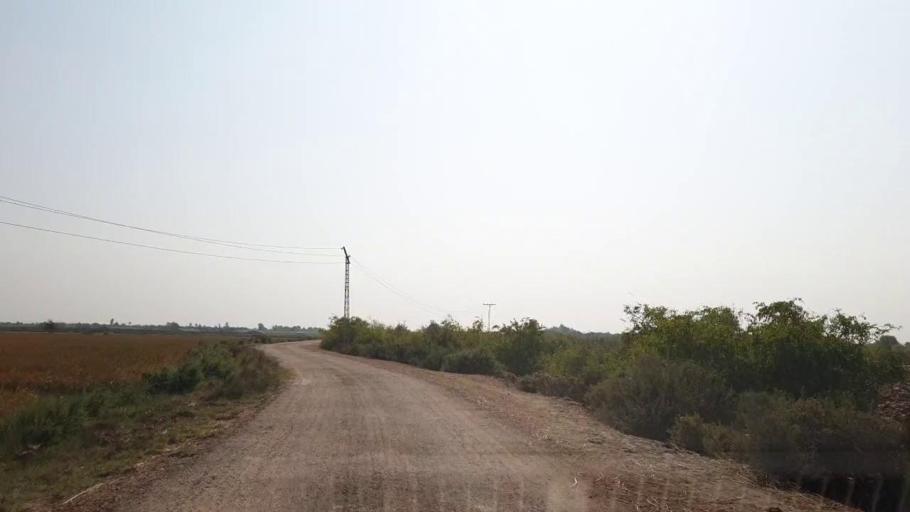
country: PK
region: Sindh
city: Tando Muhammad Khan
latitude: 25.0462
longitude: 68.4522
